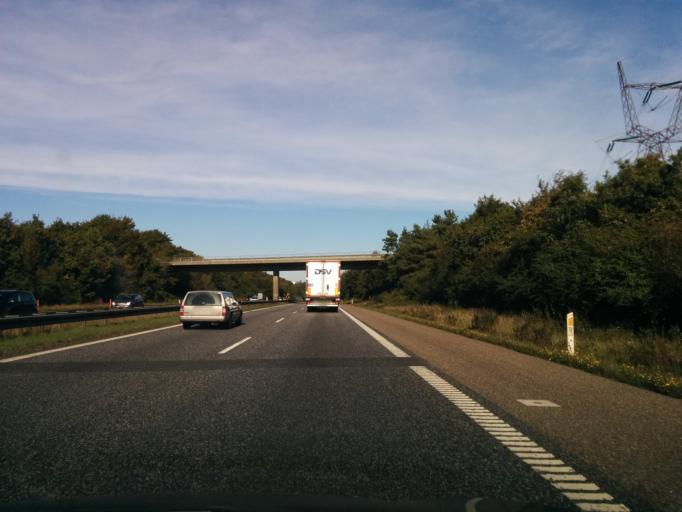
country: DK
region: South Denmark
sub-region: Kolding Kommune
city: Kolding
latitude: 55.4861
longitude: 9.4218
